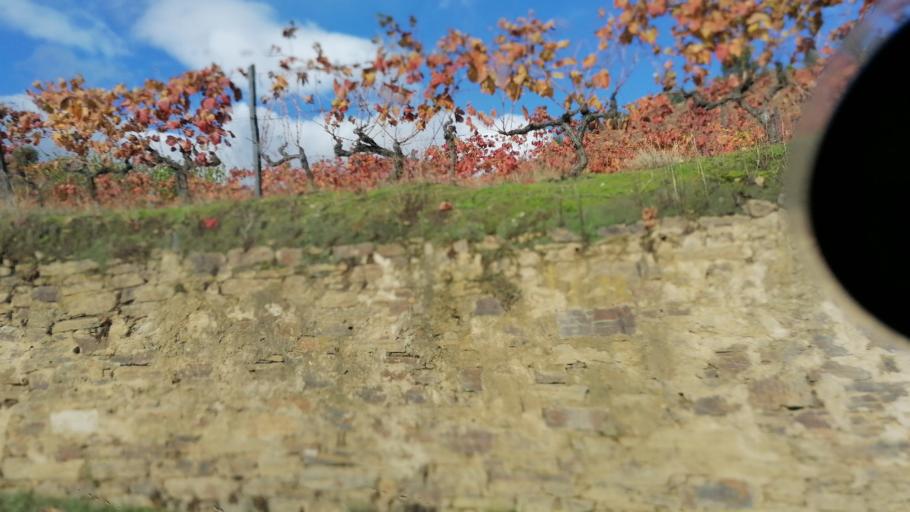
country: PT
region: Vila Real
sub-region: Peso da Regua
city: Peso da Regua
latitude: 41.1365
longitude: -7.7816
